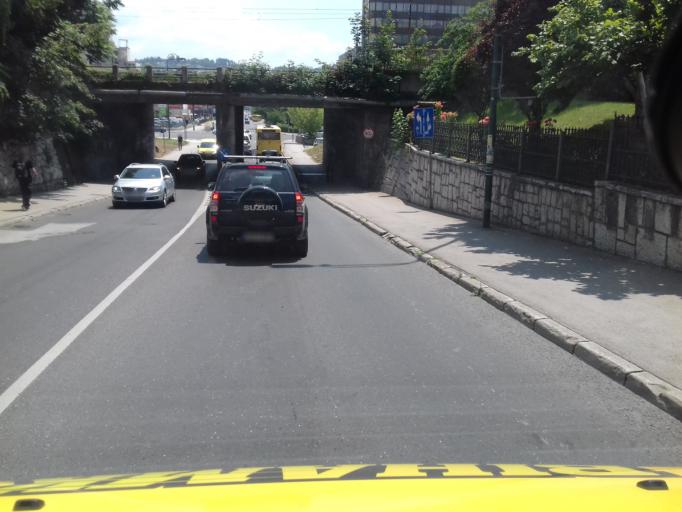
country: BA
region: Federation of Bosnia and Herzegovina
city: Kobilja Glava
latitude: 43.8588
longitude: 18.3909
